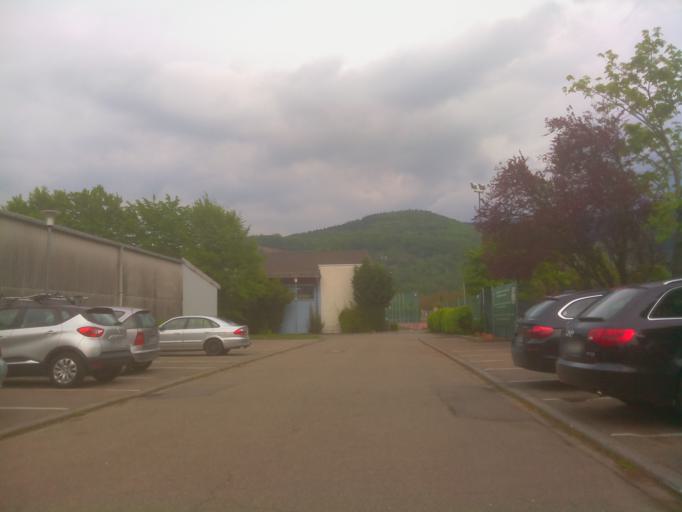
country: DE
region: Baden-Wuerttemberg
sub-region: Karlsruhe Region
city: Dossenheim
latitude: 49.4419
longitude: 8.6688
